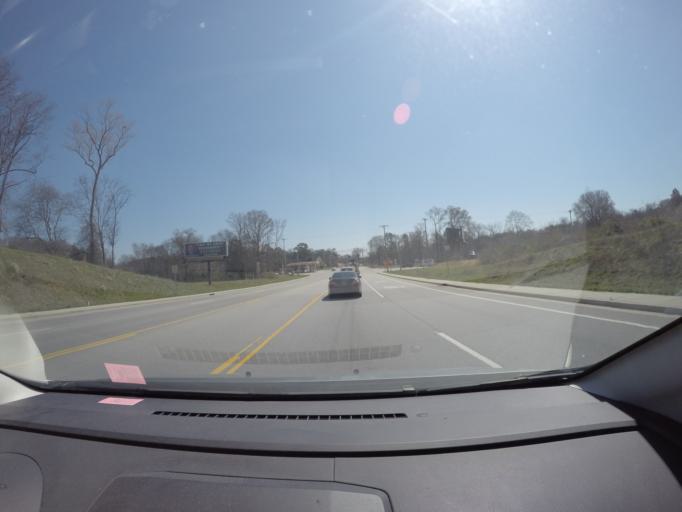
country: US
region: Tennessee
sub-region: Hamilton County
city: Collegedale
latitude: 35.0702
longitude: -85.1020
